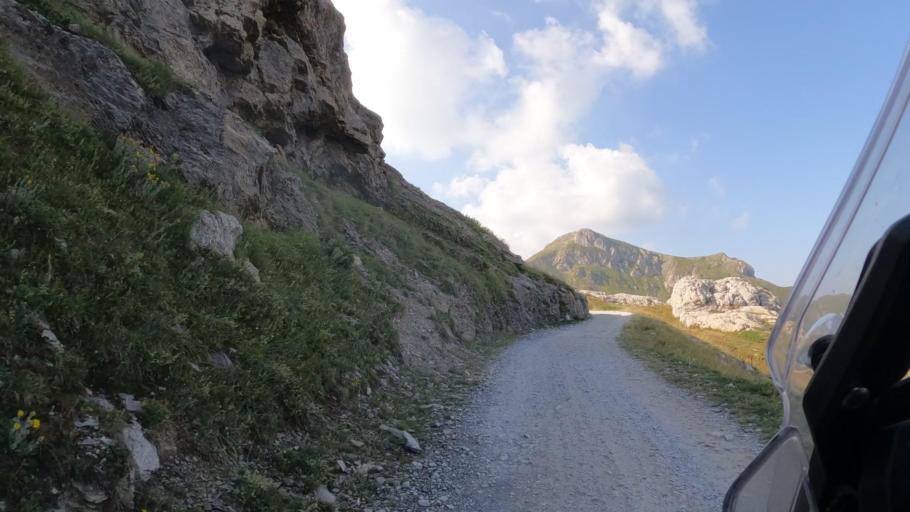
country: IT
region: Piedmont
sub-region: Provincia di Cuneo
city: Limone Piemonte
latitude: 44.1617
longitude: 7.6697
